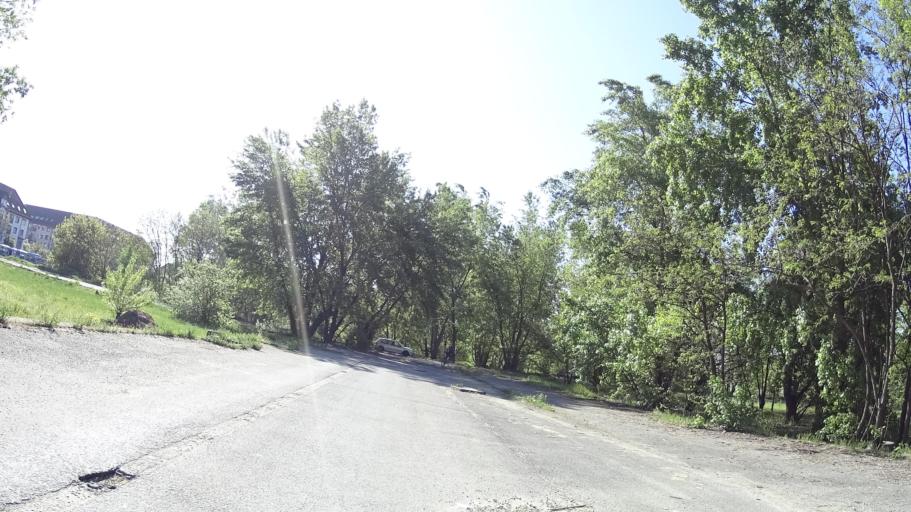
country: HU
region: Budapest
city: Budapest XXIII. keruelet
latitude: 47.4159
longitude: 19.1311
